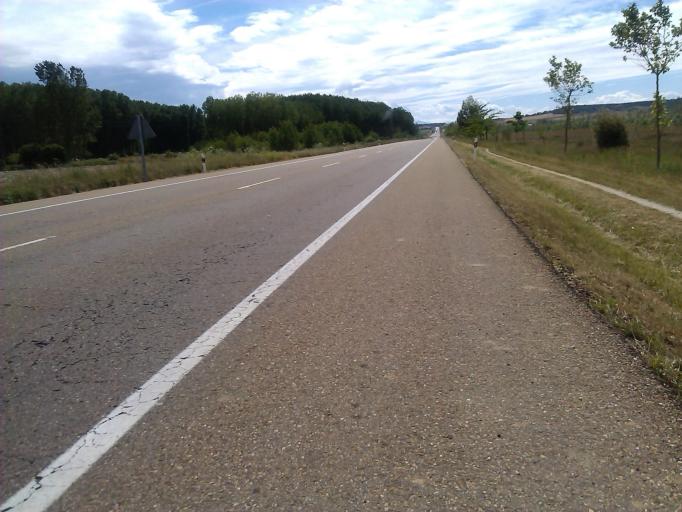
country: ES
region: Castille and Leon
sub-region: Provincia de Leon
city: Villarejo de Orbigo
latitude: 42.4549
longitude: -5.9041
